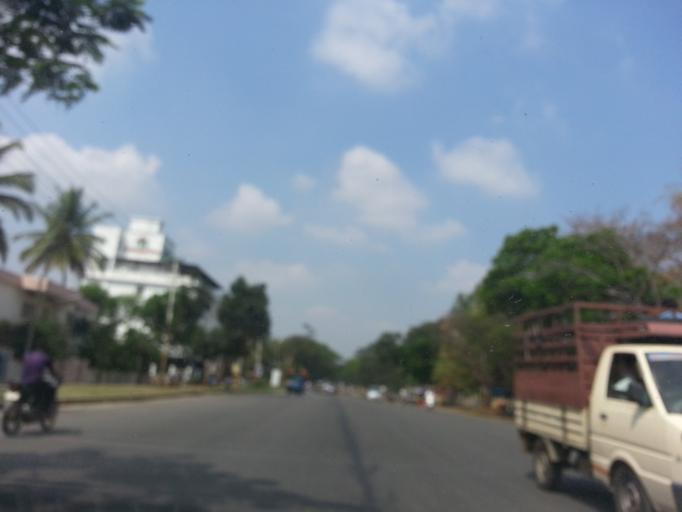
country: IN
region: Karnataka
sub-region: Mysore
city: Mysore
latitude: 12.3323
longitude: 76.6526
